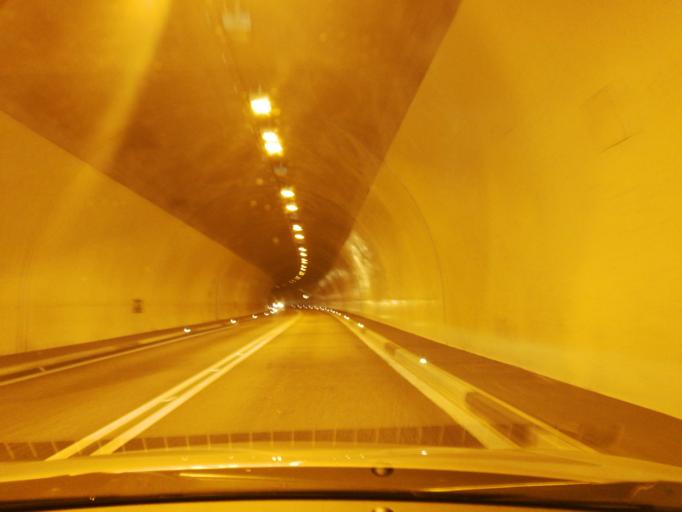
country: CH
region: Grisons
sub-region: Hinterrhein District
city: Thusis
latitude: 46.6961
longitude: 9.4491
